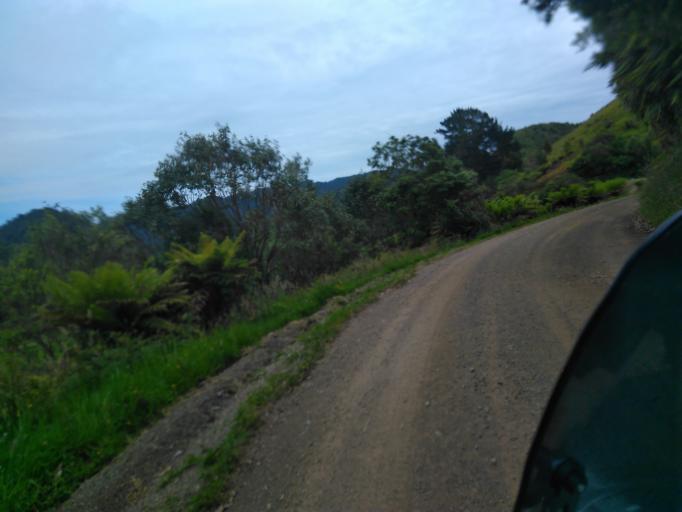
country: NZ
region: Bay of Plenty
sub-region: Opotiki District
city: Opotiki
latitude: -38.1057
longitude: 177.4993
